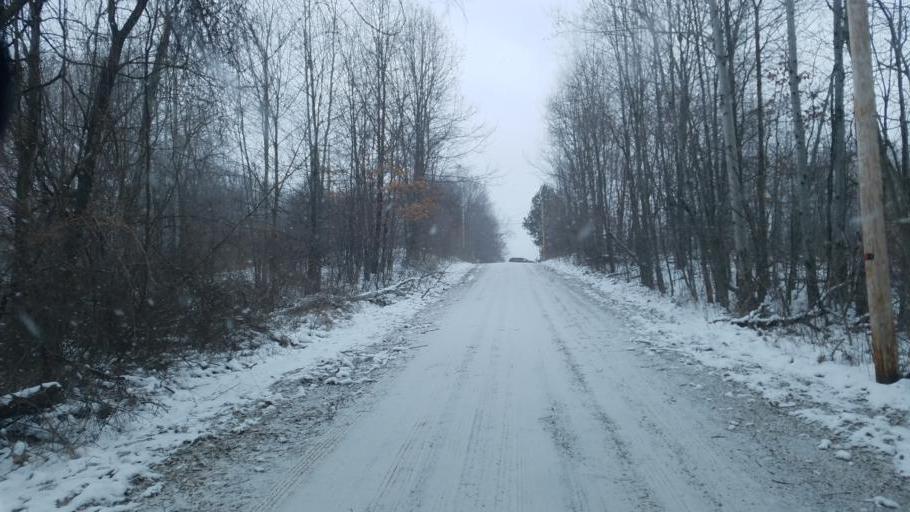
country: US
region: Pennsylvania
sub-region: Mercer County
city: Stoneboro
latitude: 41.4032
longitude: -80.0080
